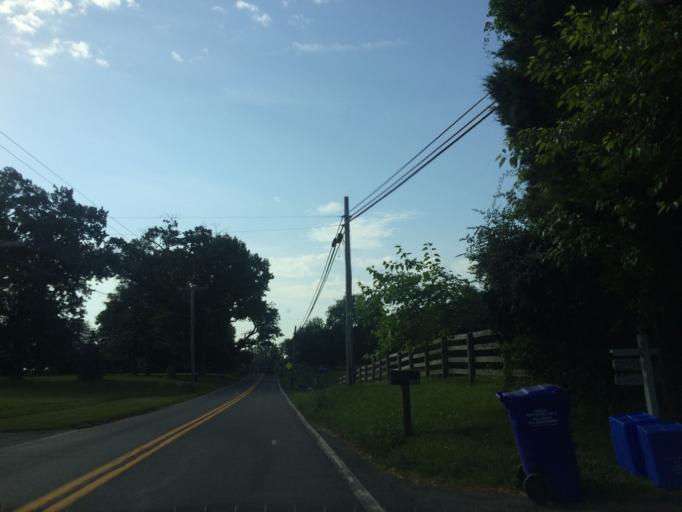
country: US
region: Maryland
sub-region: Montgomery County
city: Olney
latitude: 39.2171
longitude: -77.0539
